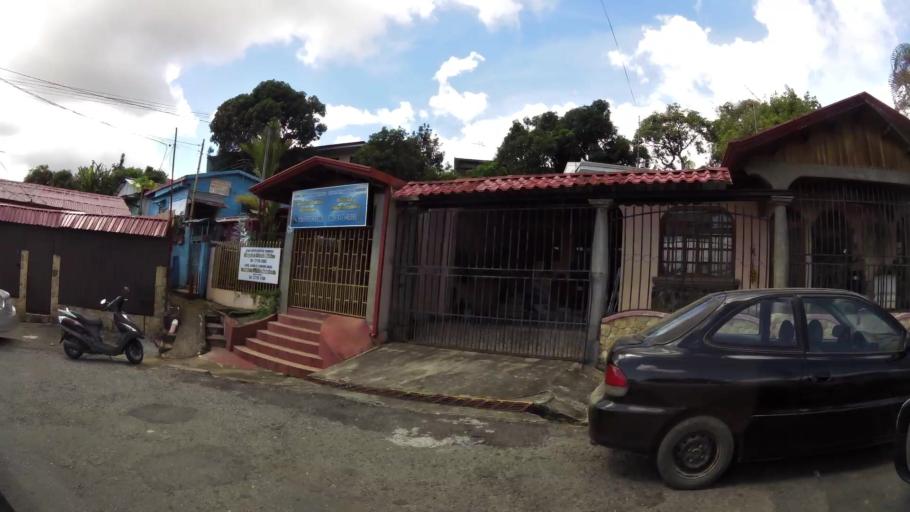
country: CR
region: San Jose
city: San Isidro
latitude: 9.3771
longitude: -83.7053
